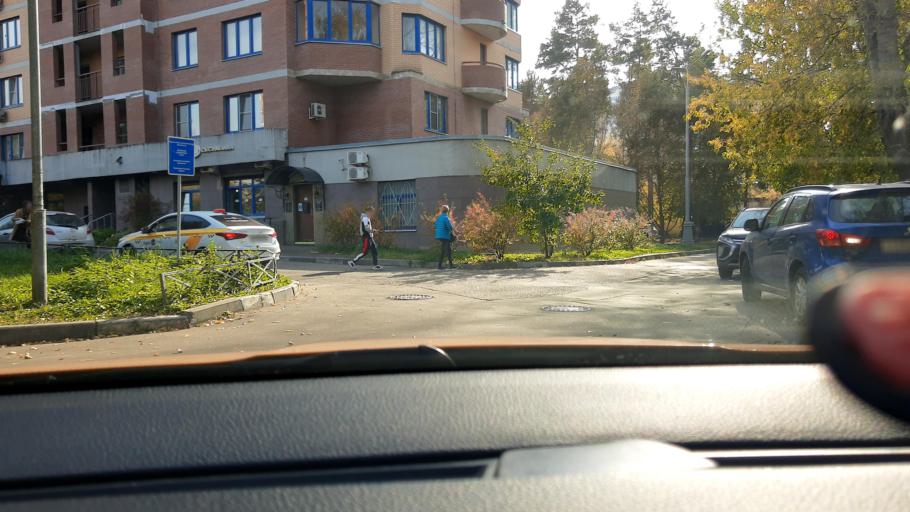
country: RU
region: Moscow
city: Leonovo
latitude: 55.8582
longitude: 37.6434
